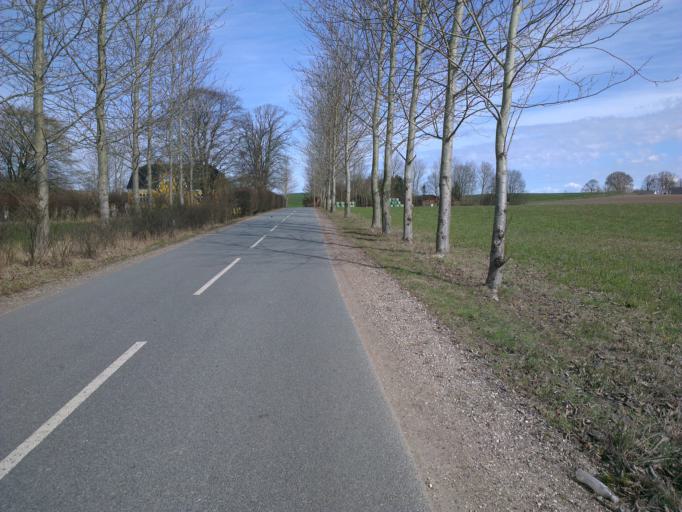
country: DK
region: Capital Region
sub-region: Egedal Kommune
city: Olstykke
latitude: 55.8410
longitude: 12.1240
